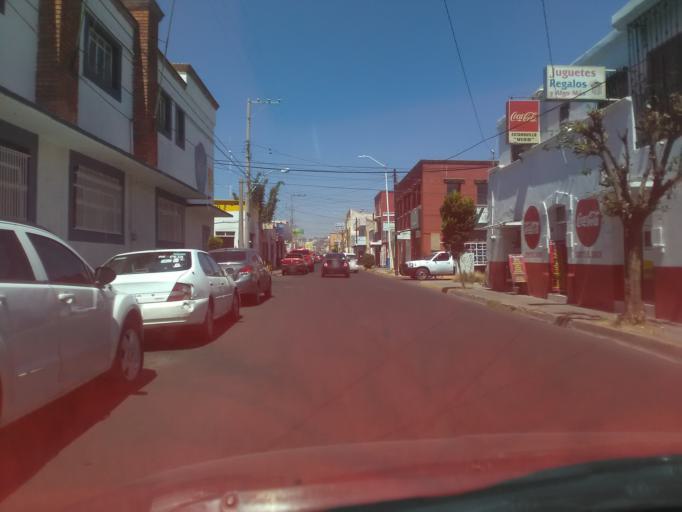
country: MX
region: Durango
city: Victoria de Durango
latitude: 24.0253
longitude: -104.6581
